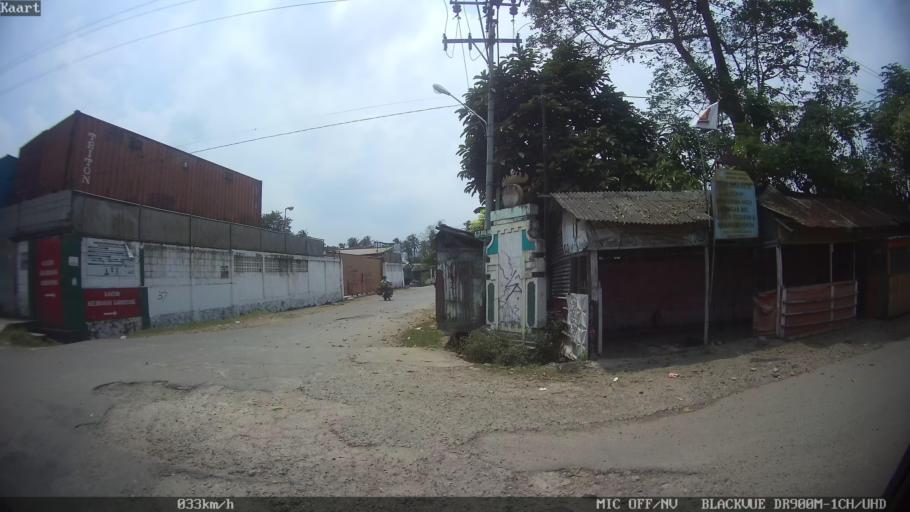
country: ID
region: Lampung
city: Bandarlampung
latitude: -5.4432
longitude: 105.2932
